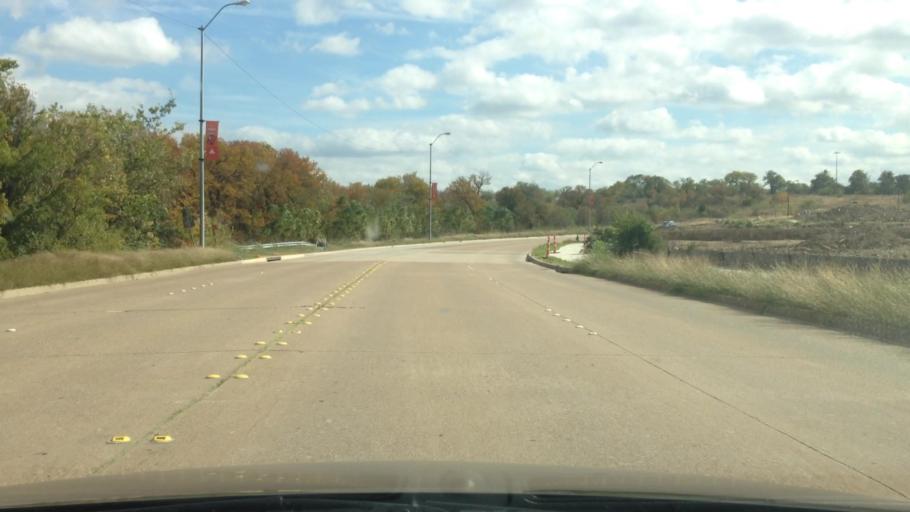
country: US
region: Texas
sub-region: Tarrant County
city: Watauga
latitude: 32.8457
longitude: -97.2765
